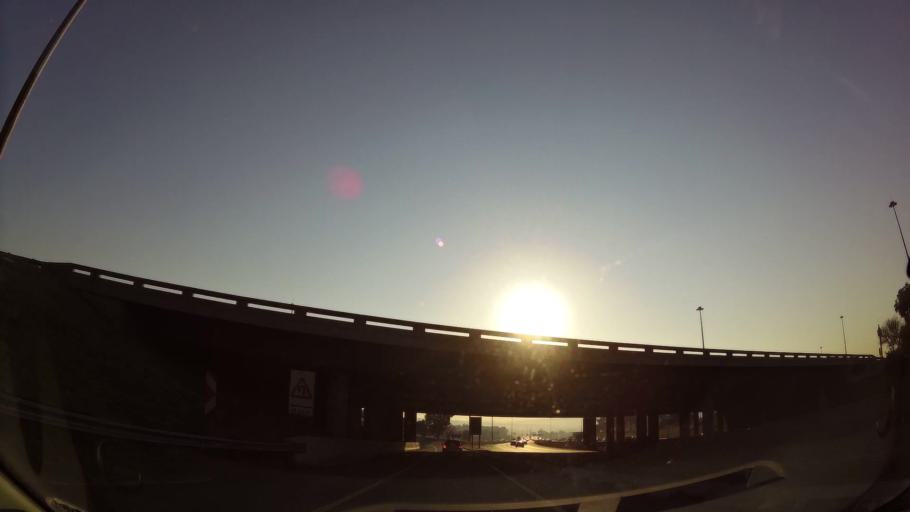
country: ZA
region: Gauteng
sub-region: City of Johannesburg Metropolitan Municipality
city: Midrand
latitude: -26.0469
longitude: 28.0956
